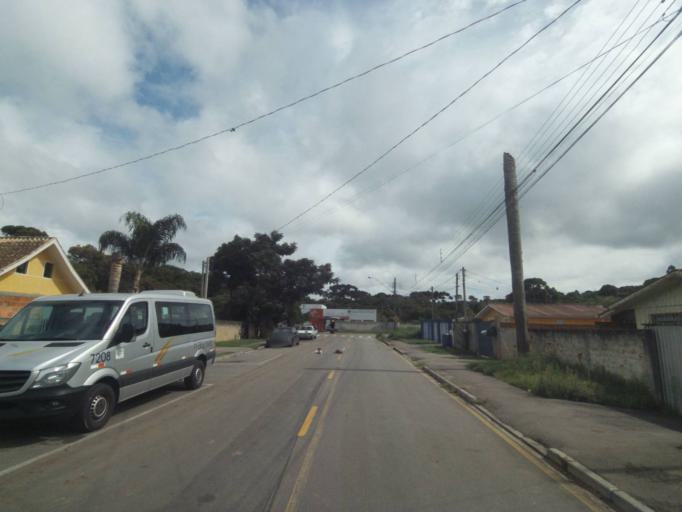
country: BR
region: Parana
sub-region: Quatro Barras
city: Quatro Barras
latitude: -25.3430
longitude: -49.0914
